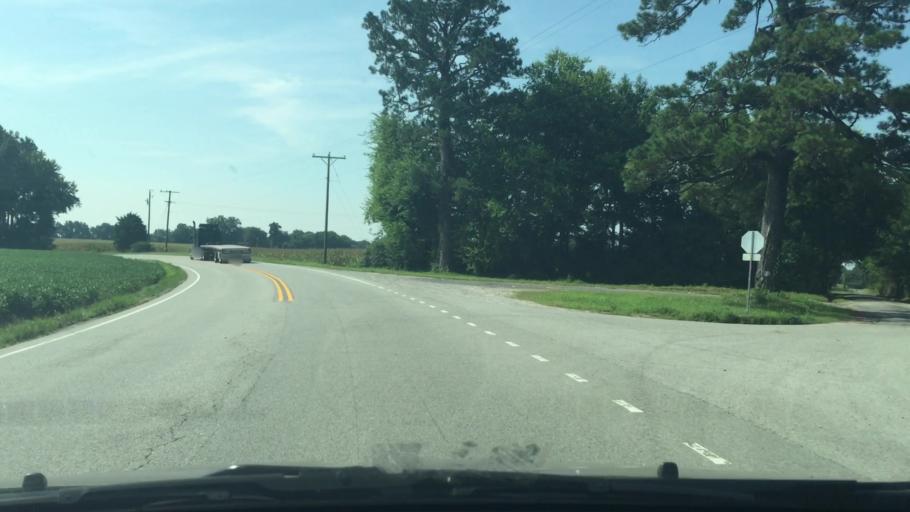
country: US
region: Virginia
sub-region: Sussex County
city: Sussex
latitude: 36.8858
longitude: -77.1546
